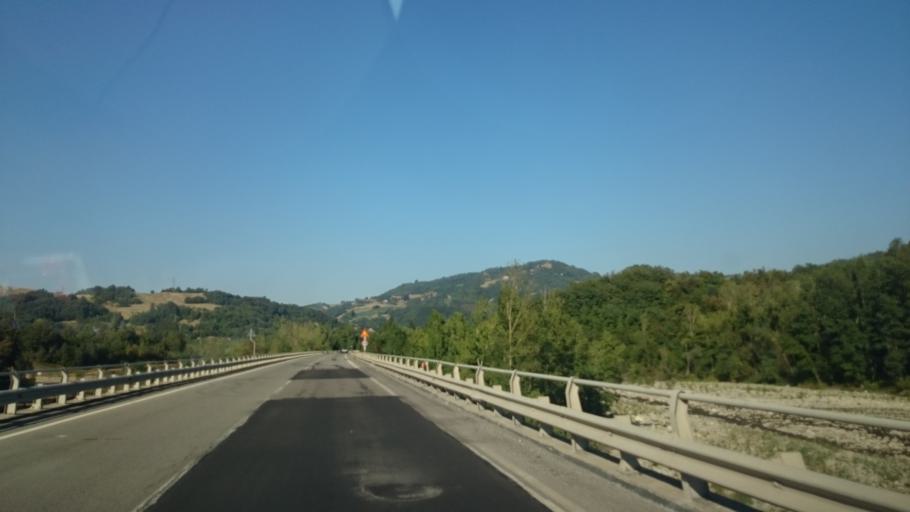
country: IT
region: Emilia-Romagna
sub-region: Provincia di Modena
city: Prignano
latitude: 44.4238
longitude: 10.6350
